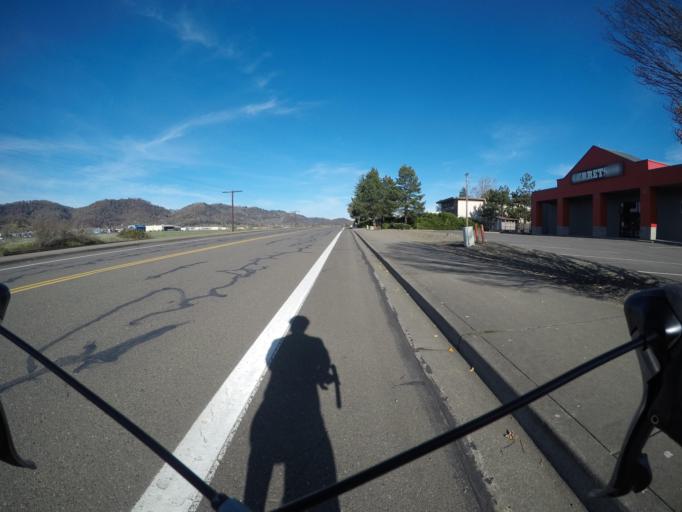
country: US
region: Oregon
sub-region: Douglas County
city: Roseburg
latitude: 43.2328
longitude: -123.3543
